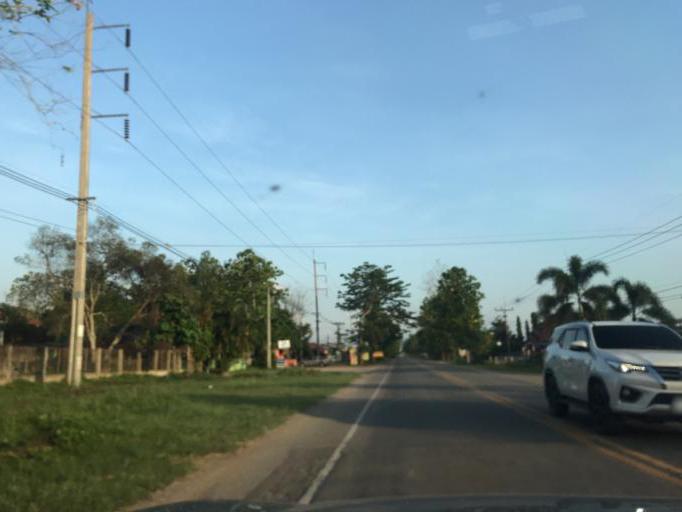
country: TH
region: Phayao
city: Chiang Kham
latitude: 19.5308
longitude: 100.2928
